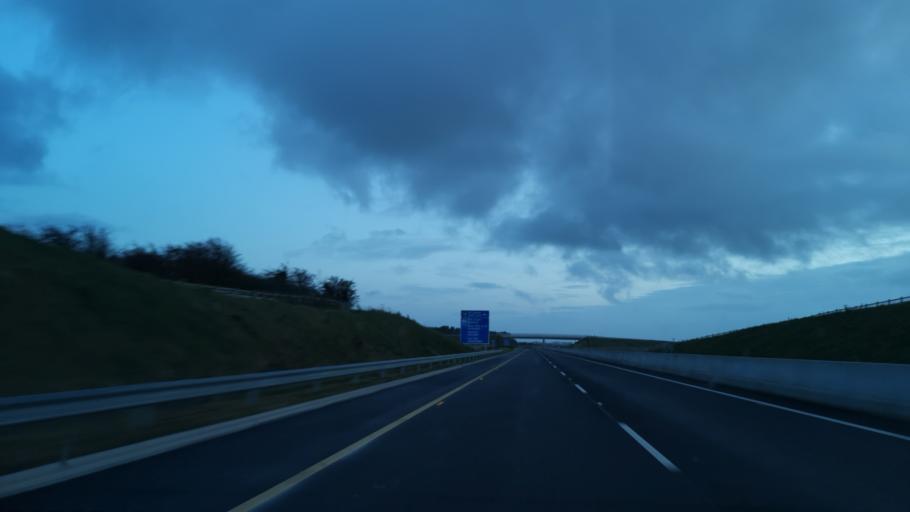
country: IE
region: Connaught
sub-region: County Galway
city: Athenry
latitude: 53.3421
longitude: -8.8016
